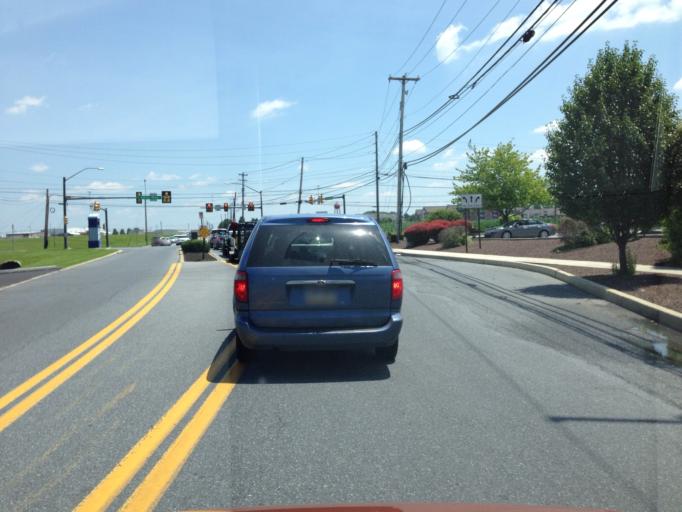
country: US
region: Pennsylvania
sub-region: Lancaster County
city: Lititz
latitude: 40.1163
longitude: -76.3068
